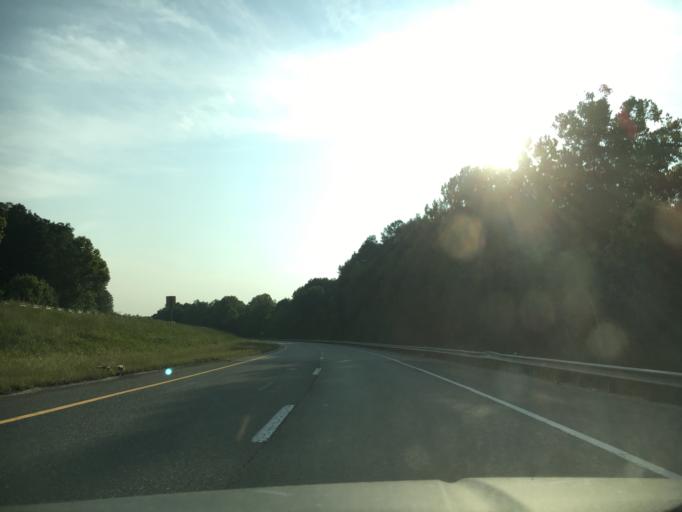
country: US
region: Virginia
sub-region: Prince Edward County
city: Farmville
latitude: 37.2791
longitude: -78.3612
